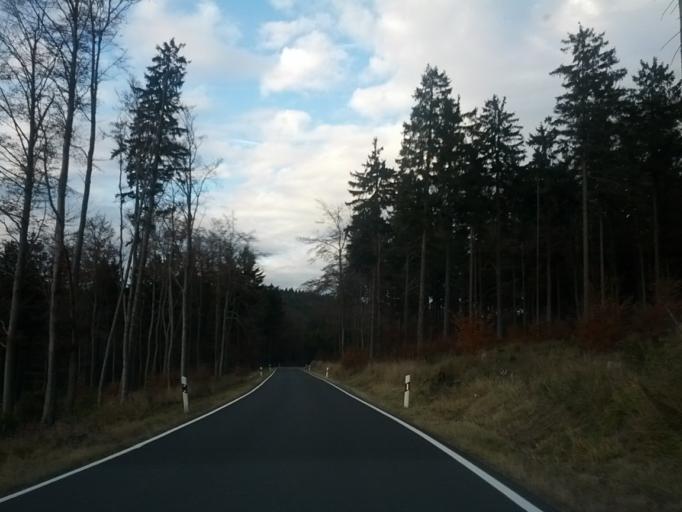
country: DE
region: Thuringia
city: Steinbach
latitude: 50.8493
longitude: 10.4051
